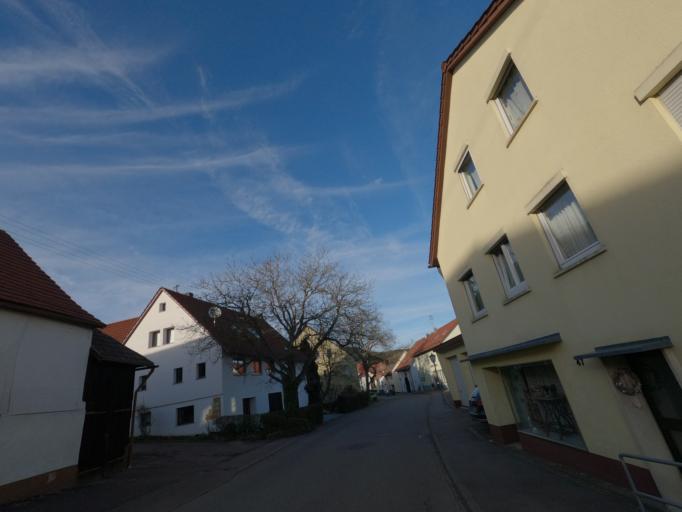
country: DE
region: Baden-Wuerttemberg
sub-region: Regierungsbezirk Stuttgart
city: Waldstetten
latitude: 48.7287
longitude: 9.8104
